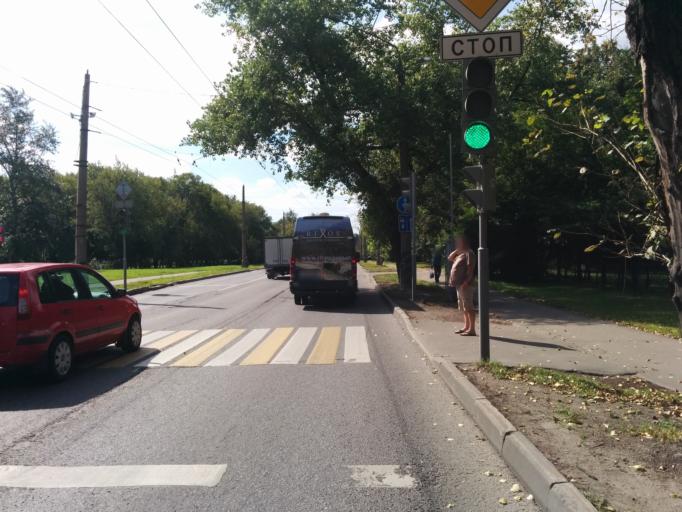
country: RU
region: Moscow
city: Ostankinskiy
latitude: 55.8166
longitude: 37.6175
